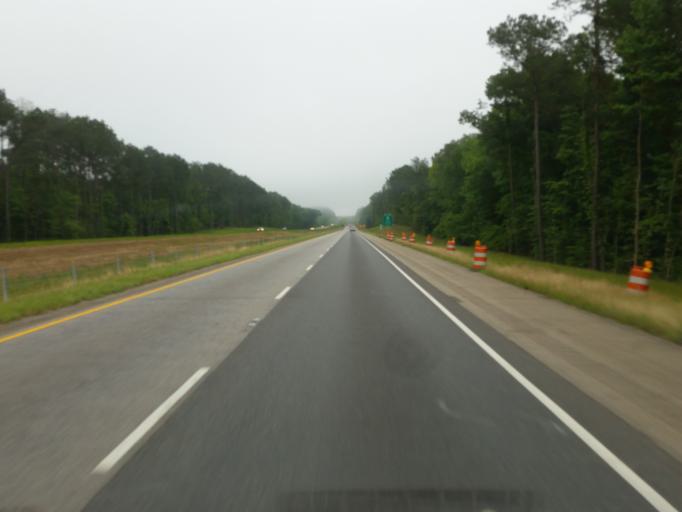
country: US
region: Louisiana
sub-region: Webster Parish
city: Minden
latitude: 32.5668
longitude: -93.1835
